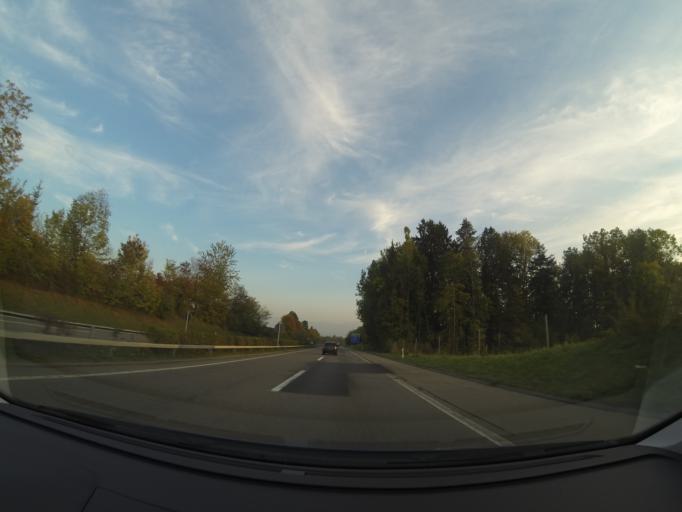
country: CH
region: Zurich
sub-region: Bezirk Hinwil
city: Bubikon
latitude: 47.2801
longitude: 8.8250
